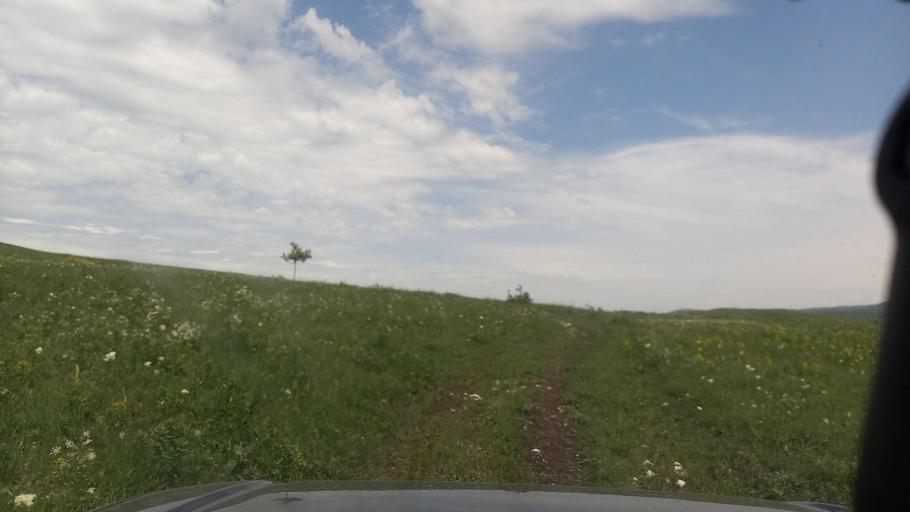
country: RU
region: Karachayevo-Cherkesiya
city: Pregradnaya
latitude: 44.0697
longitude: 41.2923
